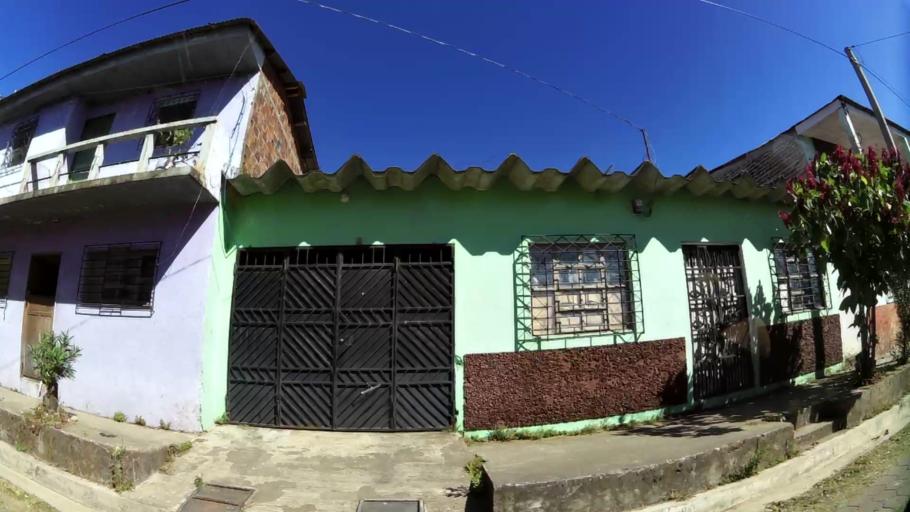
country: SV
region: Sonsonate
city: Juayua
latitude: 13.8428
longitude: -89.7442
